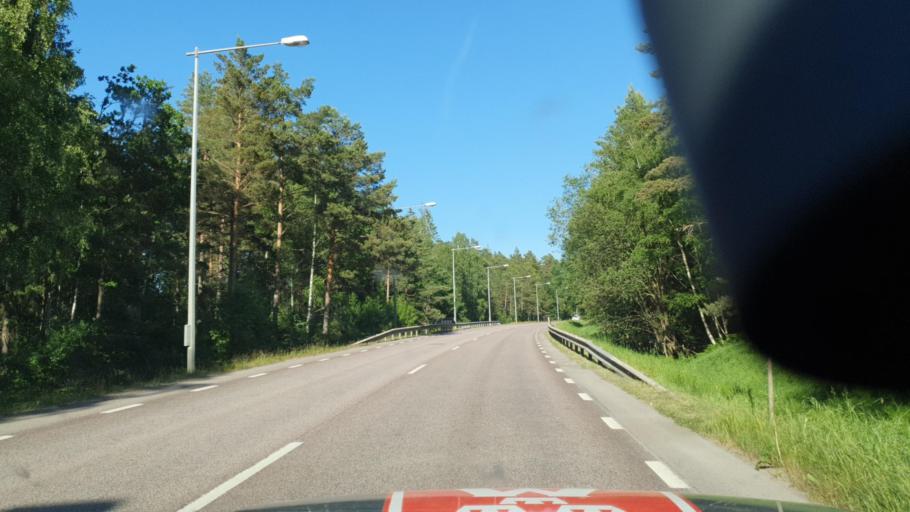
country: SE
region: Kalmar
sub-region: Nybro Kommun
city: Nybro
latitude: 56.7557
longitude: 15.9062
